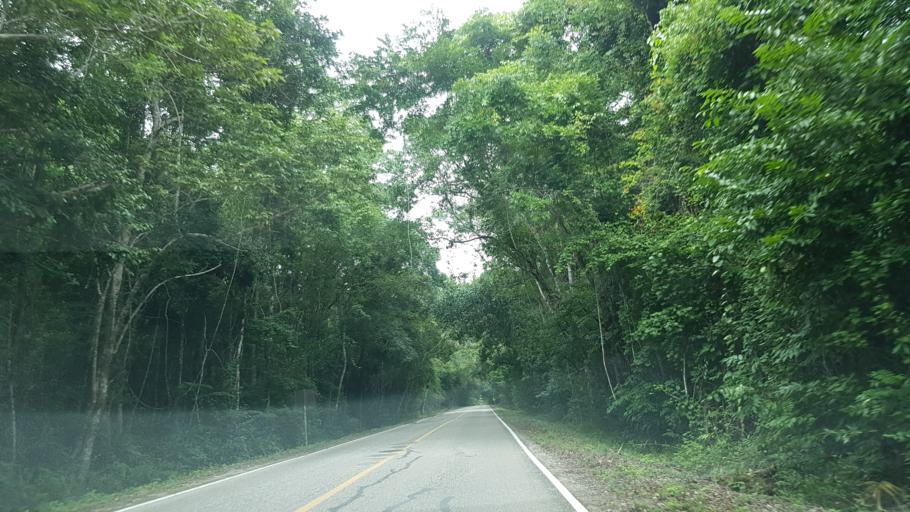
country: GT
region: Peten
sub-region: Municipio de San Jose
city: San Jose
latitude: 17.1837
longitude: -89.6341
